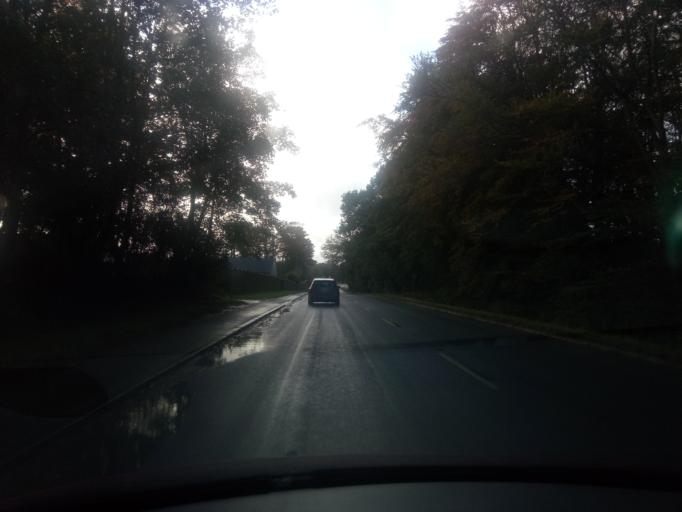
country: GB
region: England
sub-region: Cumbria
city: Carlisle
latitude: 54.9357
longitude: -2.9451
